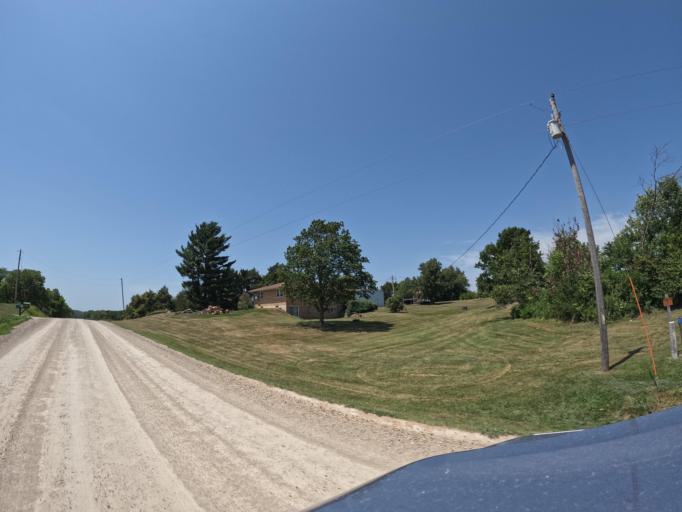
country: US
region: Iowa
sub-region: Henry County
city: Mount Pleasant
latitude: 40.9450
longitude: -91.6651
